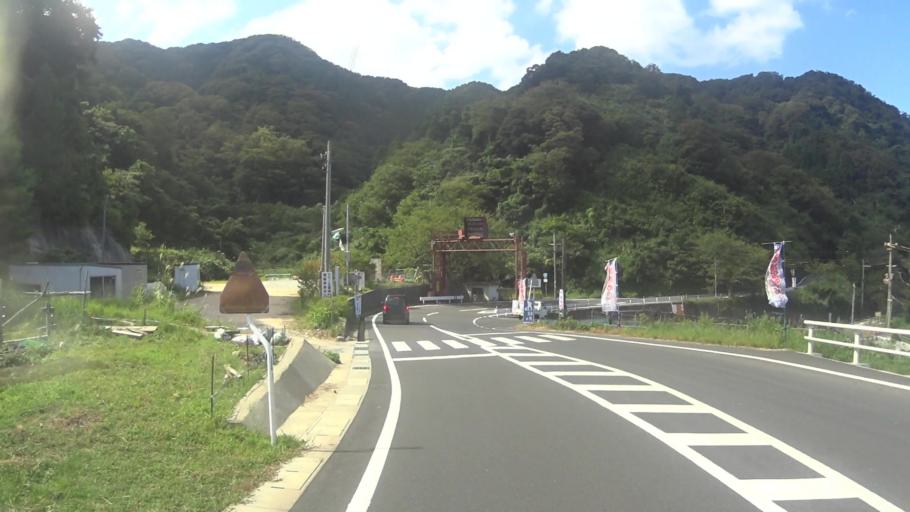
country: JP
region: Kyoto
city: Miyazu
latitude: 35.7510
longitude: 135.2503
